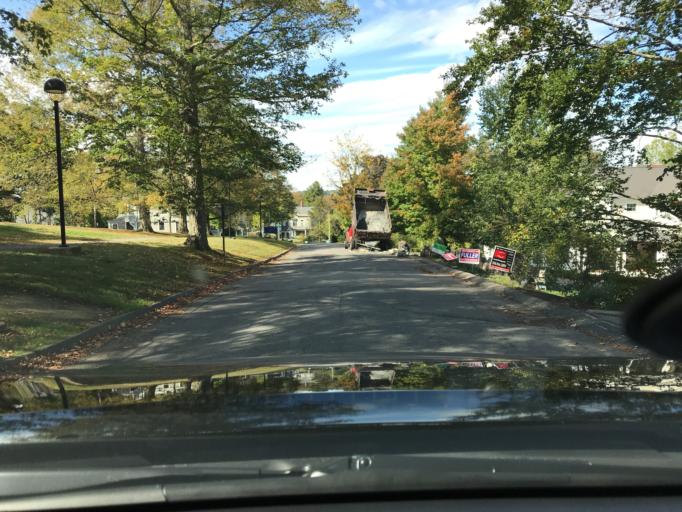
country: US
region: Massachusetts
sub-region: Middlesex County
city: Newton
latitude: 42.3268
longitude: -71.1915
